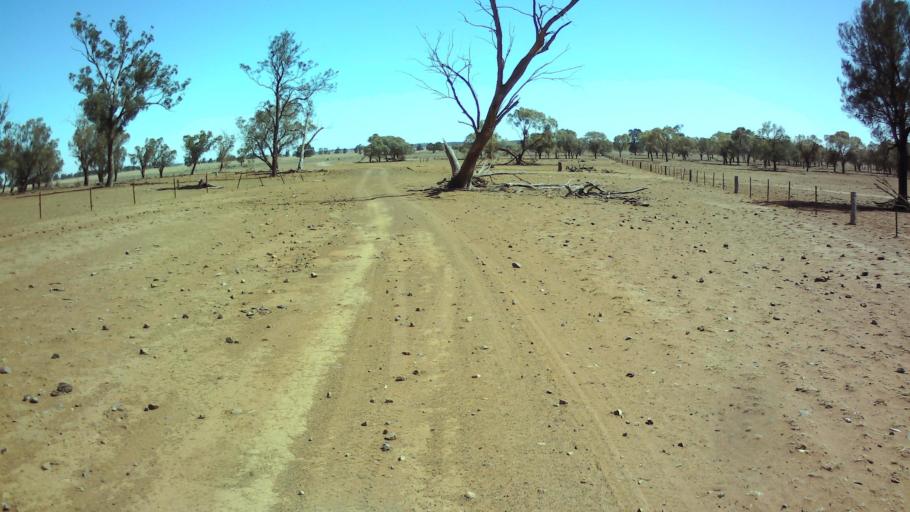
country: AU
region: New South Wales
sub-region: Forbes
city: Forbes
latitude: -33.7279
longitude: 147.6658
